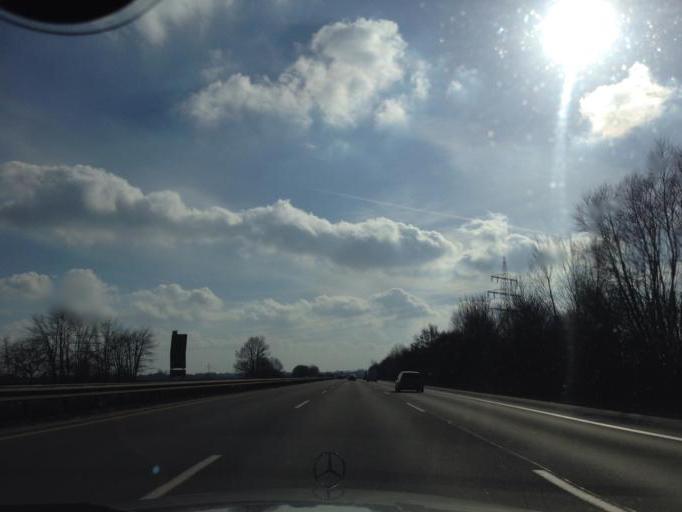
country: DE
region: Hamburg
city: Harburg
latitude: 53.4385
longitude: 10.0311
